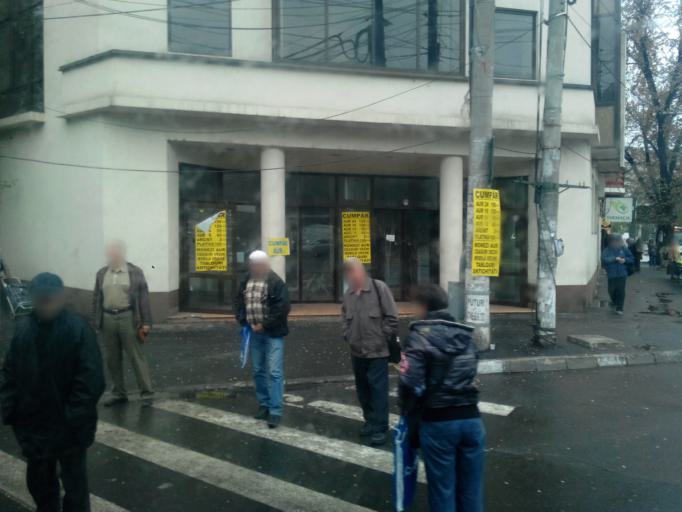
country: RO
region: Bucuresti
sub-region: Municipiul Bucuresti
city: Bucharest
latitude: 44.4462
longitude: 26.1348
